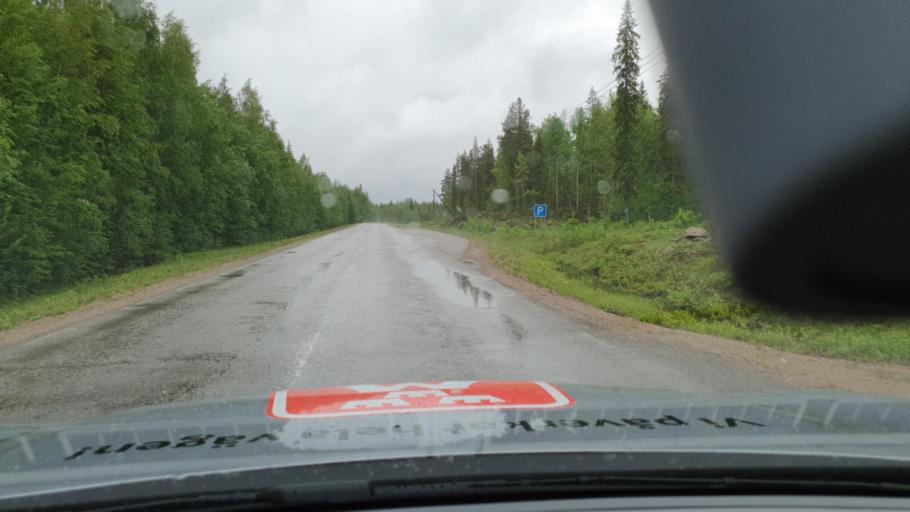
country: SE
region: Norrbotten
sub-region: Overkalix Kommun
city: OEverkalix
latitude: 66.4420
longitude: 23.0380
